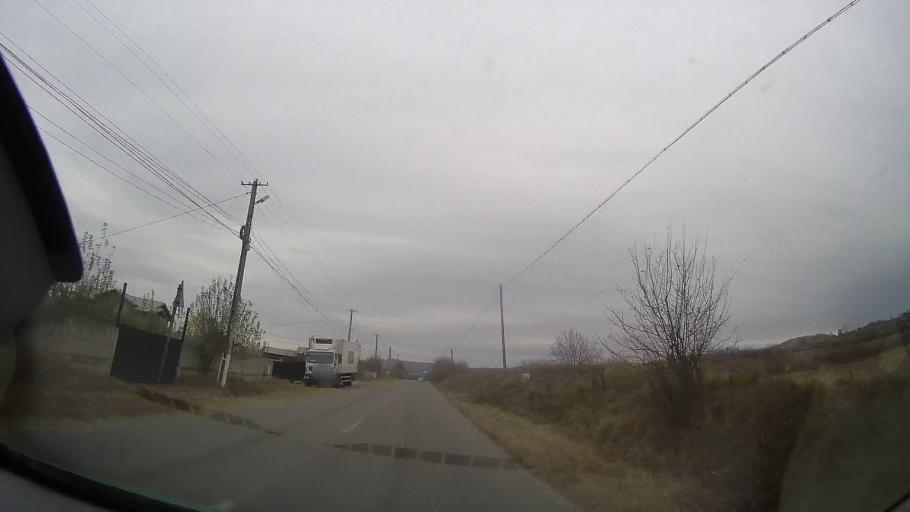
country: RO
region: Prahova
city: Mocesti
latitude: 45.0629
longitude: 26.2471
